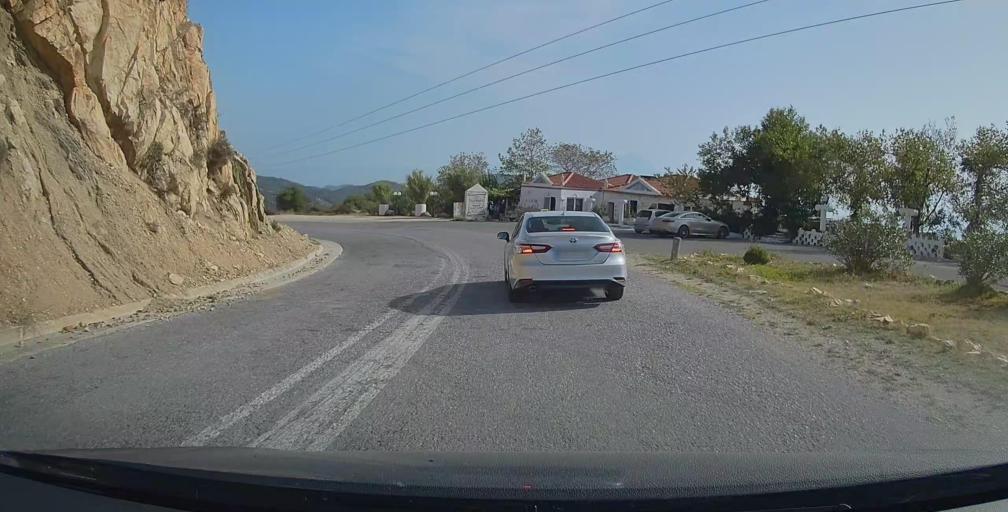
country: GR
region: Central Macedonia
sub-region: Nomos Chalkidikis
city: Sykia
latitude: 39.9822
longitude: 23.9603
